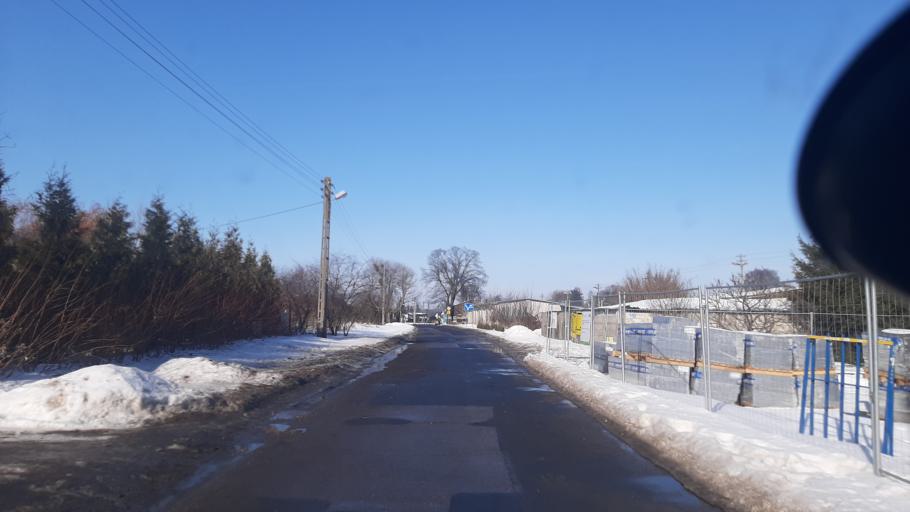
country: PL
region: Lublin Voivodeship
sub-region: Powiat lubelski
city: Wojciechow
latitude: 51.2864
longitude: 22.2828
